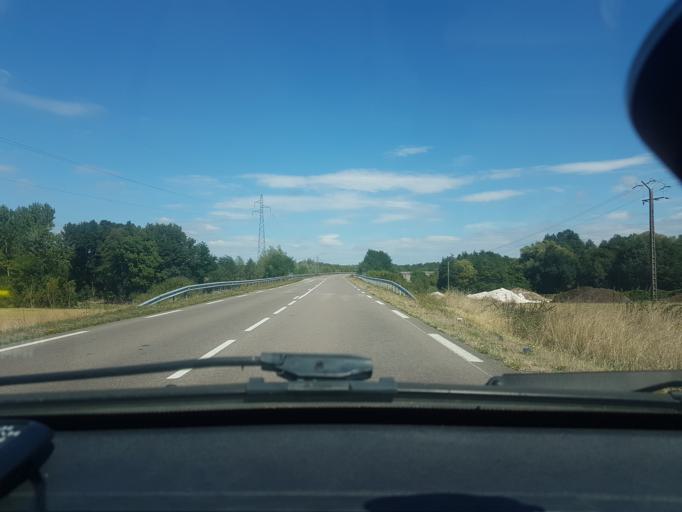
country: FR
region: Franche-Comte
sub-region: Departement de la Haute-Saone
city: Gray-la-Ville
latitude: 47.4264
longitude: 5.5280
